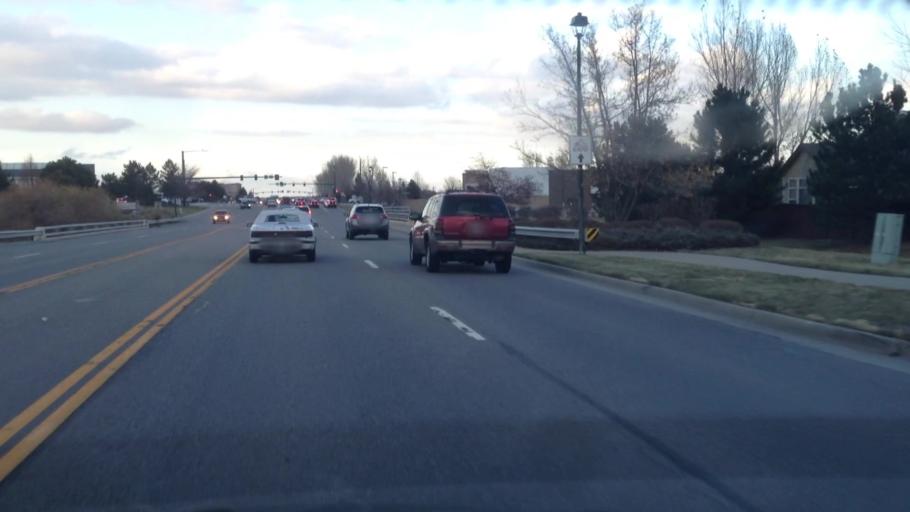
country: US
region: Colorado
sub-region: Douglas County
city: Stonegate
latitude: 39.5314
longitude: -104.7934
